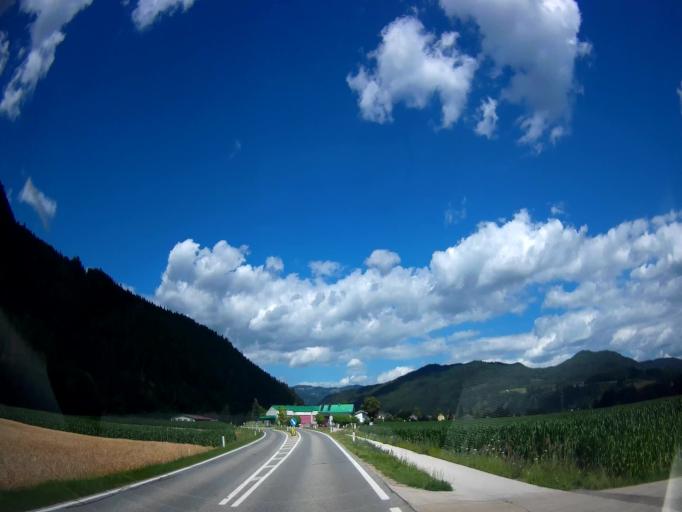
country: AT
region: Carinthia
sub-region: Politischer Bezirk Klagenfurt Land
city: Poggersdorf
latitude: 46.6815
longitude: 14.4810
